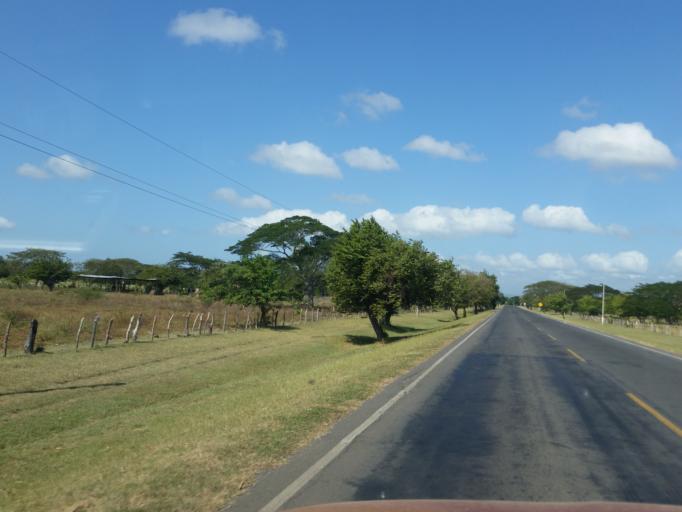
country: NI
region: Granada
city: Nandaime
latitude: 11.6953
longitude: -85.9977
